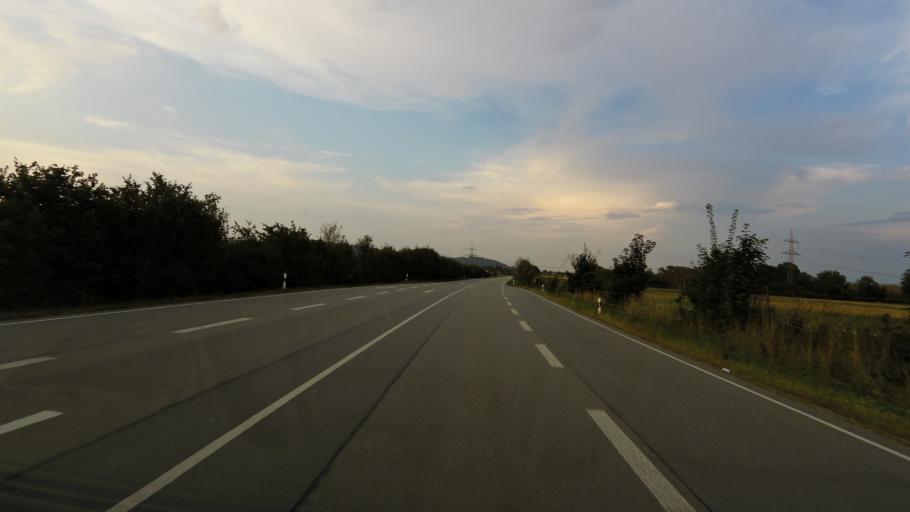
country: AT
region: Upper Austria
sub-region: Politischer Bezirk Braunau am Inn
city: Braunau am Inn
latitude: 48.2773
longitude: 13.0566
